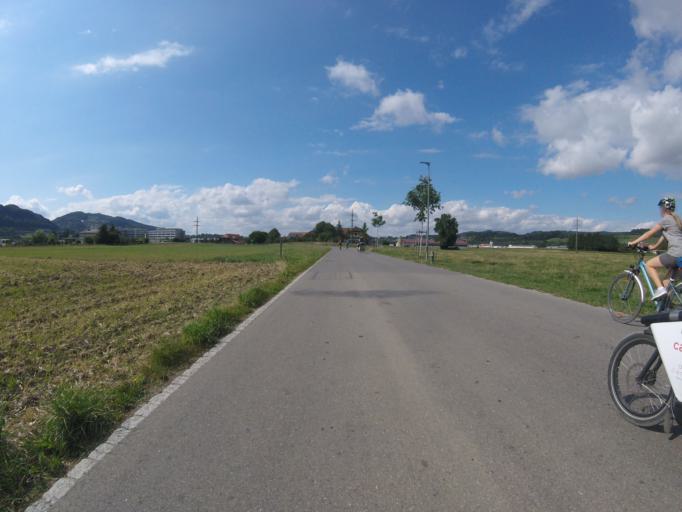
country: CH
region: Bern
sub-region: Bern-Mittelland District
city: Belp
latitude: 46.9029
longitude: 7.5013
